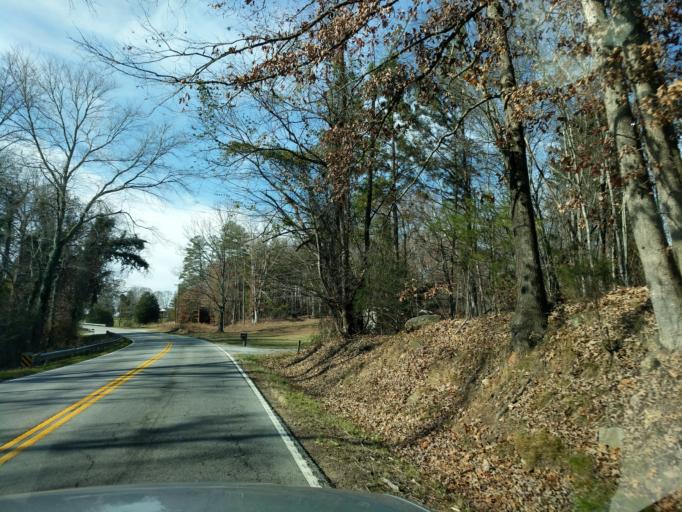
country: US
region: South Carolina
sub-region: Pickens County
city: Pickens
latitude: 34.8618
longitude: -82.7730
